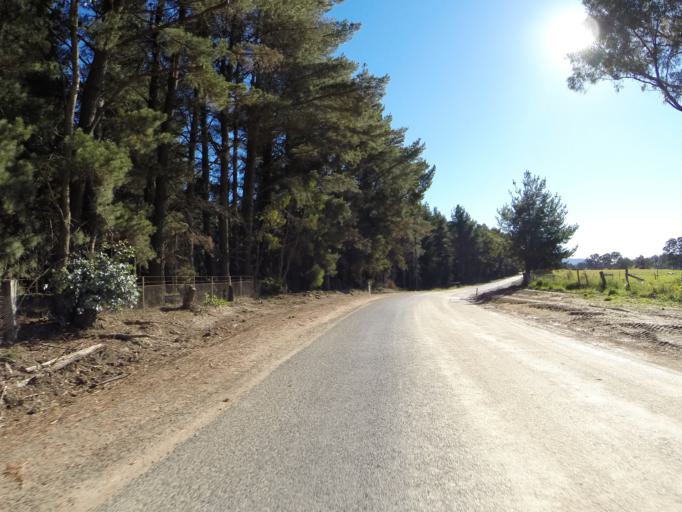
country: AU
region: New South Wales
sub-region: Oberon
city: Oberon
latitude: -33.6028
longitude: 149.8452
